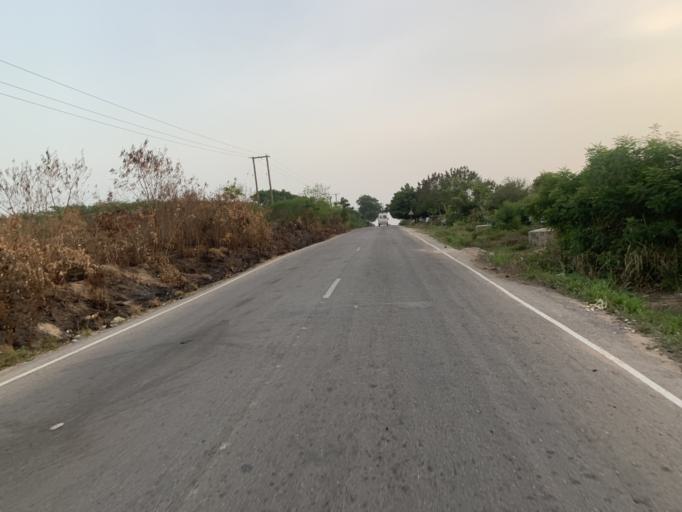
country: GH
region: Central
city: Winneba
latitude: 5.3609
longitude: -0.6095
